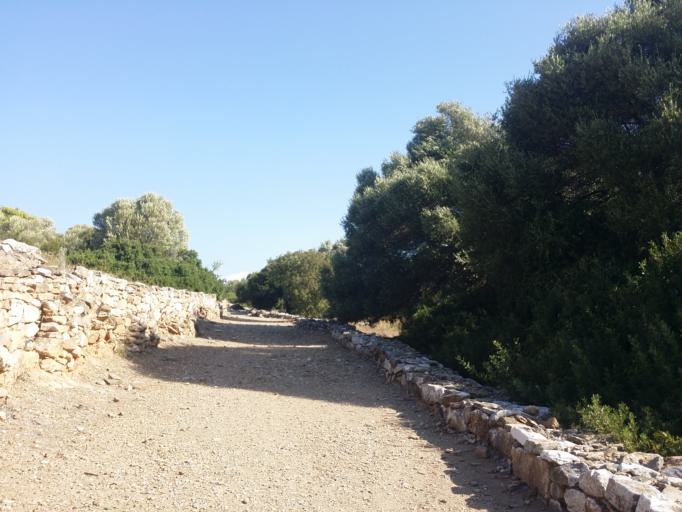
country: GR
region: Attica
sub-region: Nomarchia Anatolikis Attikis
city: Kato Soulion
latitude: 38.2163
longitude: 24.0268
